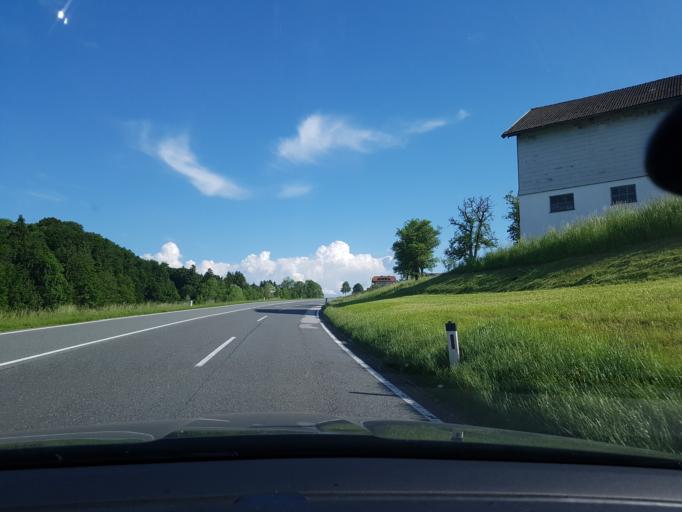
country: AT
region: Salzburg
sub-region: Politischer Bezirk Salzburg-Umgebung
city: Obertrum am See
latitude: 47.9294
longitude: 13.0821
